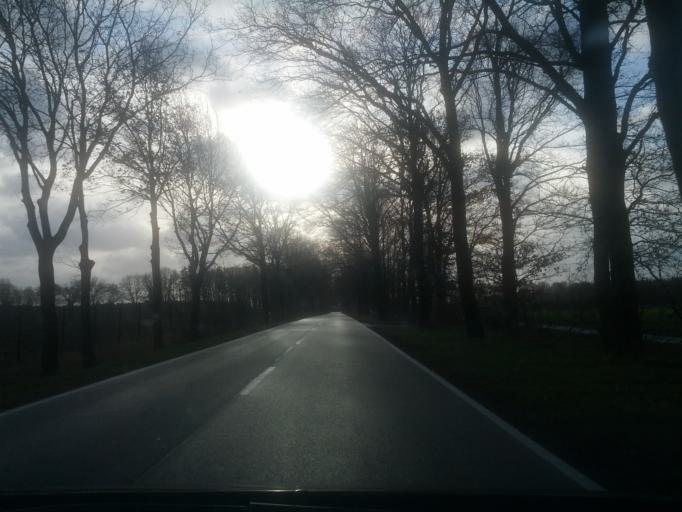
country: DE
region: Lower Saxony
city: Hamersen
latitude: 53.2438
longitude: 9.4841
